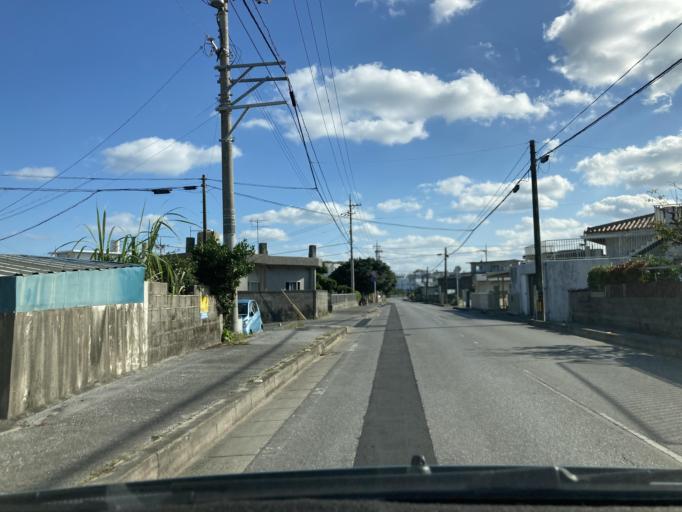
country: JP
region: Okinawa
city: Katsuren-haebaru
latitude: 26.3150
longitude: 127.9095
